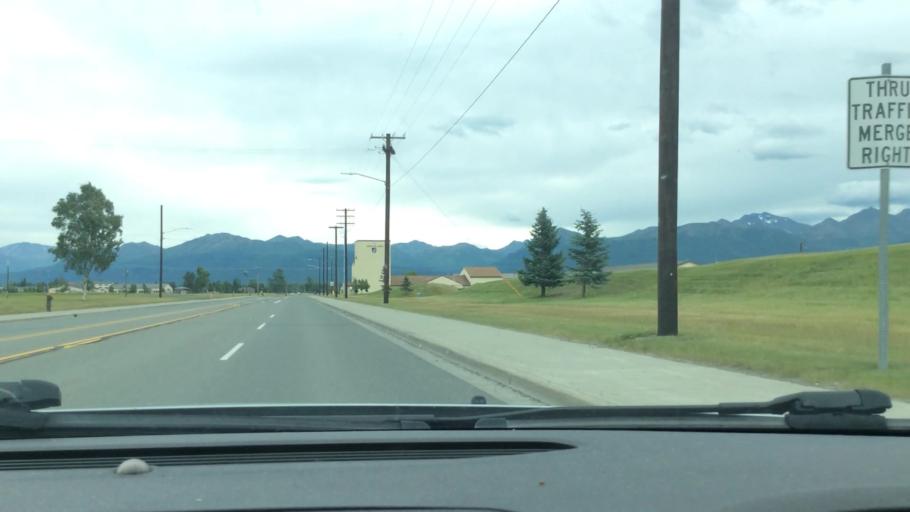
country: US
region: Alaska
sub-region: Anchorage Municipality
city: Anchorage
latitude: 61.2371
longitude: -149.8373
